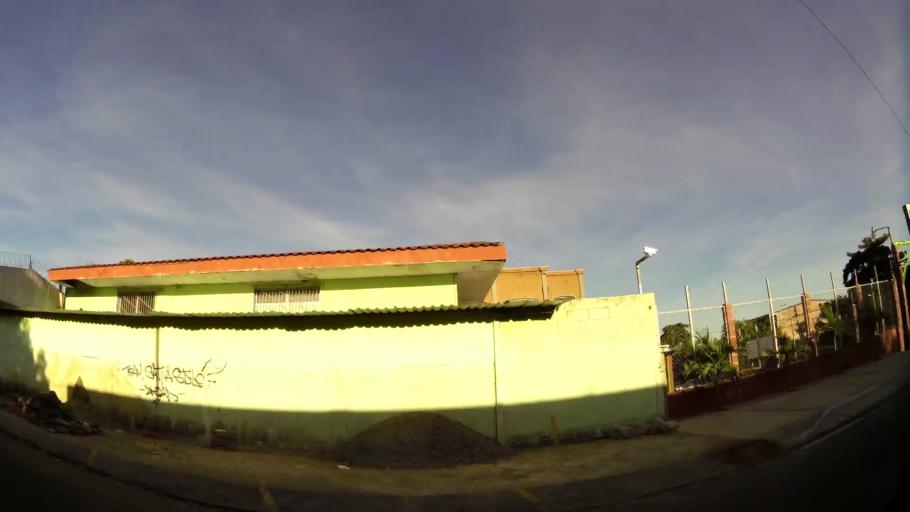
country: SV
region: San Miguel
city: San Miguel
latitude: 13.4578
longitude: -88.1627
